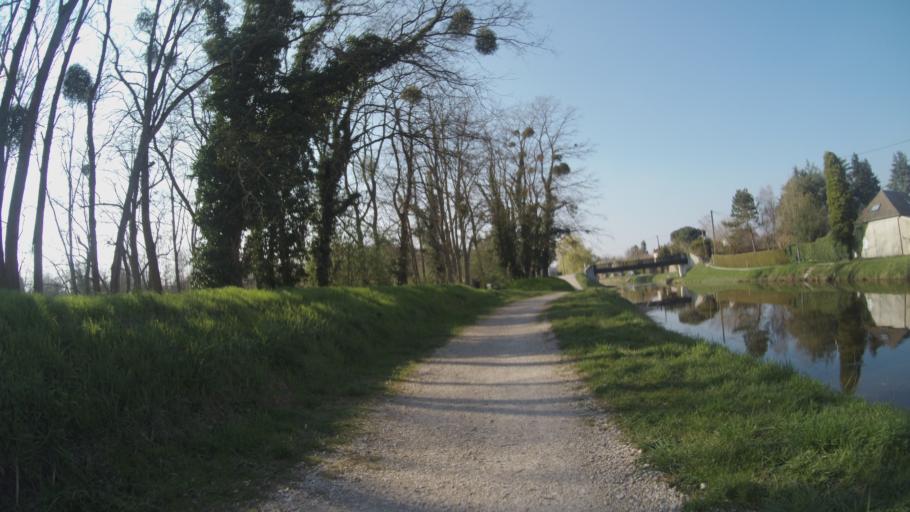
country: FR
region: Centre
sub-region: Departement du Loiret
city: Checy
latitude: 47.8946
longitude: 2.0019
